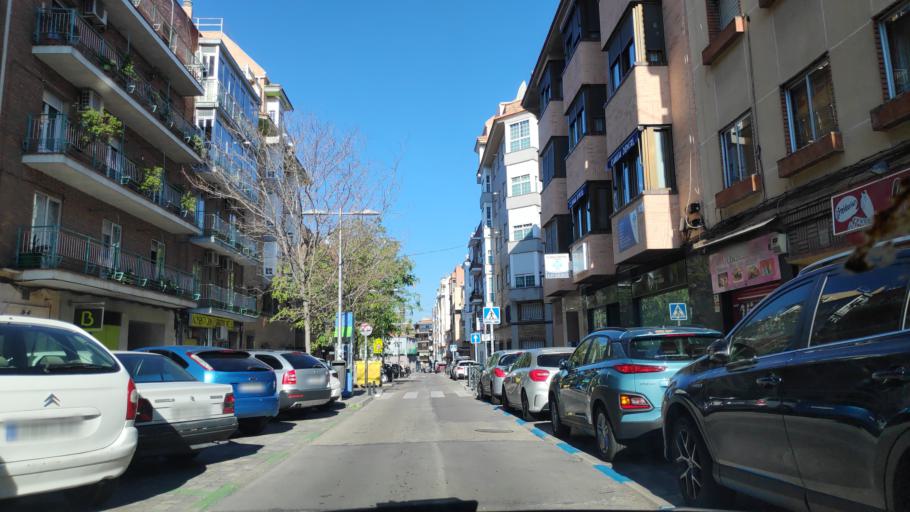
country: ES
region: Madrid
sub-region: Provincia de Madrid
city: Tetuan de las Victorias
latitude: 40.4668
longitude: -3.6967
